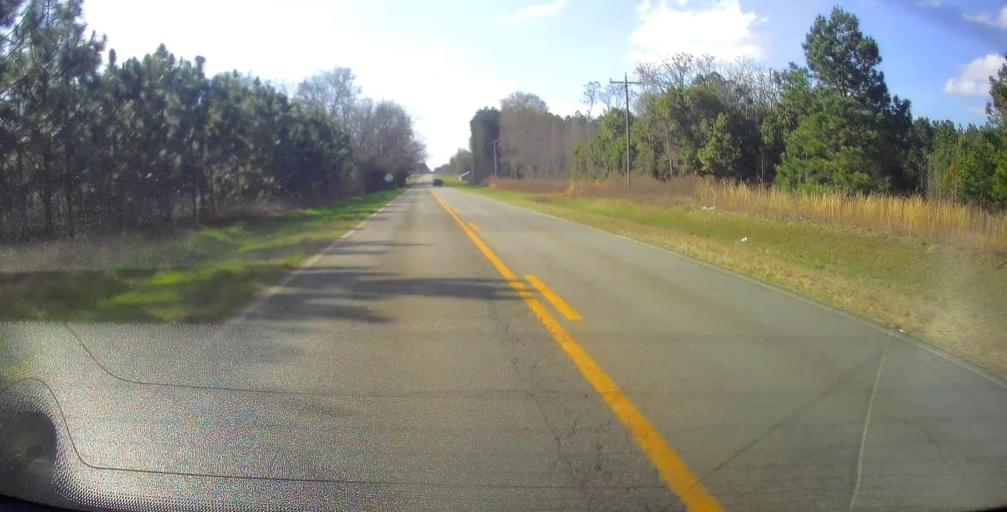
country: US
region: Georgia
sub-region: Laurens County
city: Dublin
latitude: 32.5619
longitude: -83.0146
